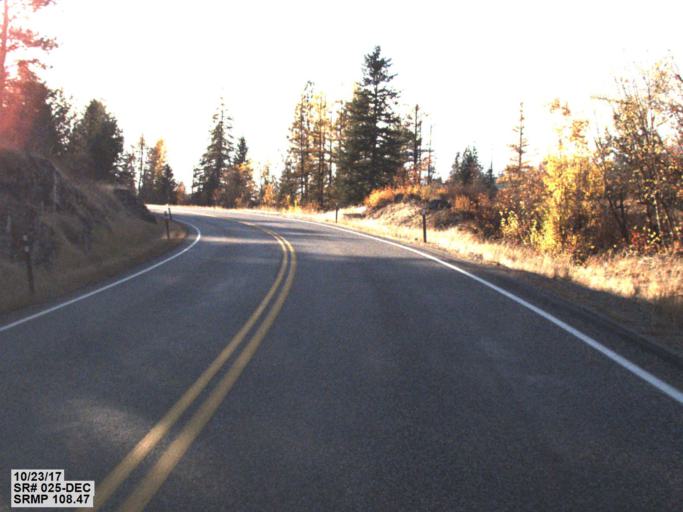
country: CA
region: British Columbia
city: Rossland
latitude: 48.8741
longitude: -117.8522
